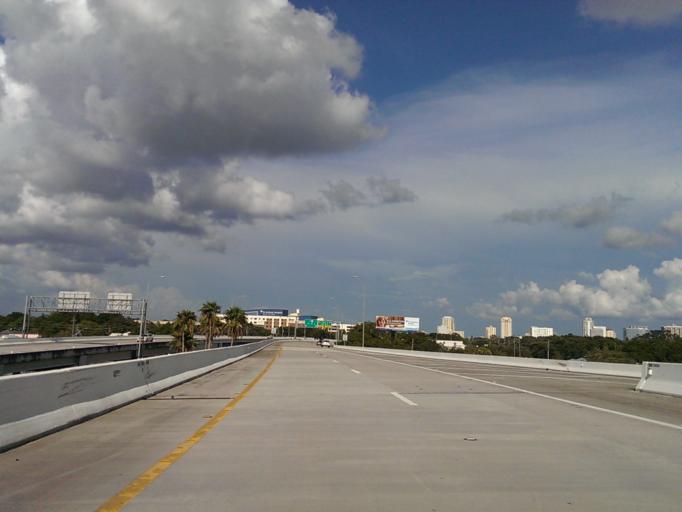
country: US
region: Florida
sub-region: Pinellas County
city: Saint Petersburg
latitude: 27.7767
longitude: -82.6570
